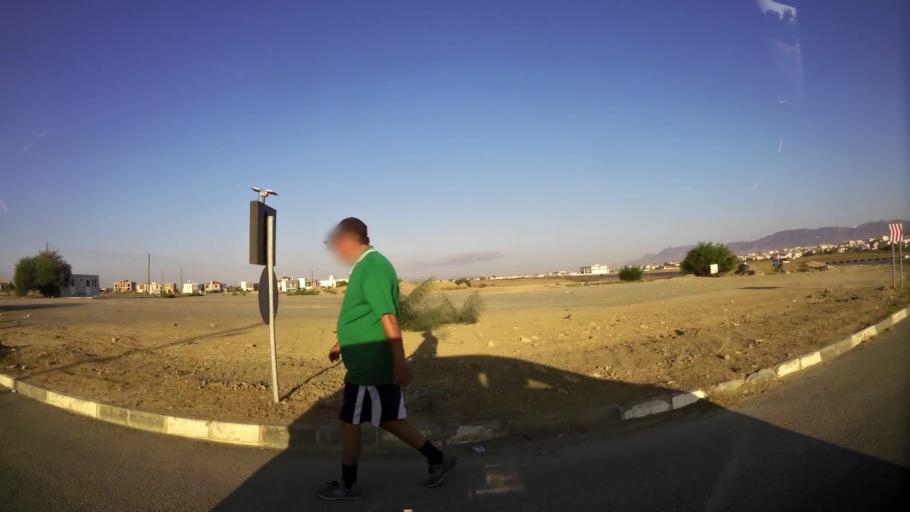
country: CY
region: Lefkosia
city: Nicosia
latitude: 35.1956
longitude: 33.3173
